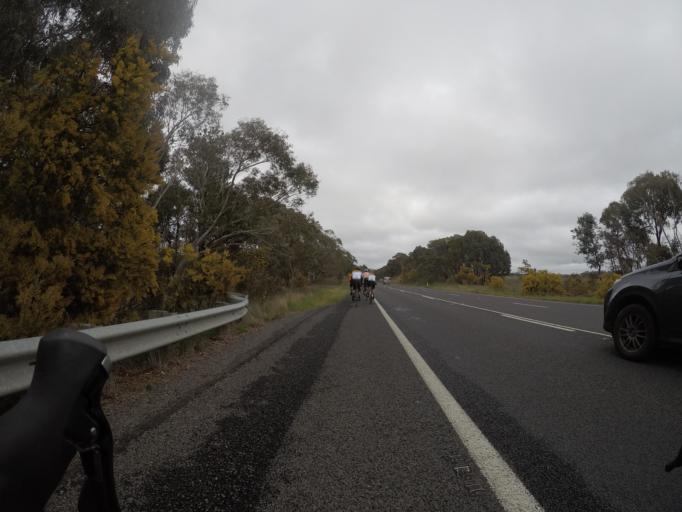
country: AU
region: New South Wales
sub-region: Lithgow
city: Portland
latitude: -33.4493
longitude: 150.0168
